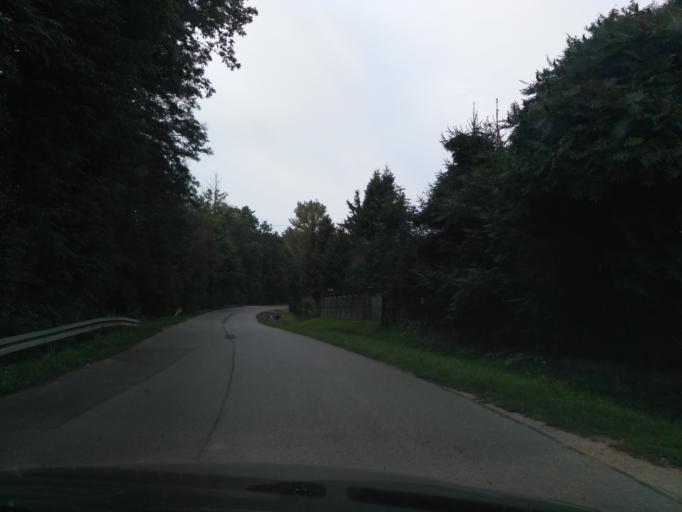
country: PL
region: Subcarpathian Voivodeship
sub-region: Powiat rzeszowski
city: Trzciana
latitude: 50.0410
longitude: 21.8347
